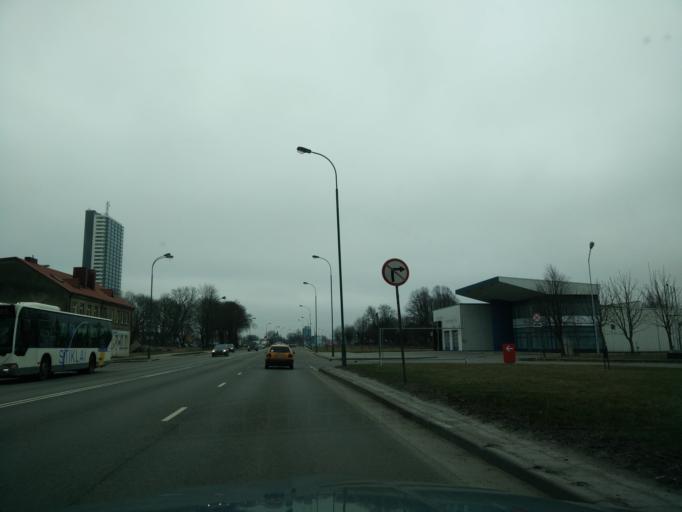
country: LT
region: Klaipedos apskritis
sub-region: Klaipeda
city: Klaipeda
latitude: 55.6941
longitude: 21.1406
